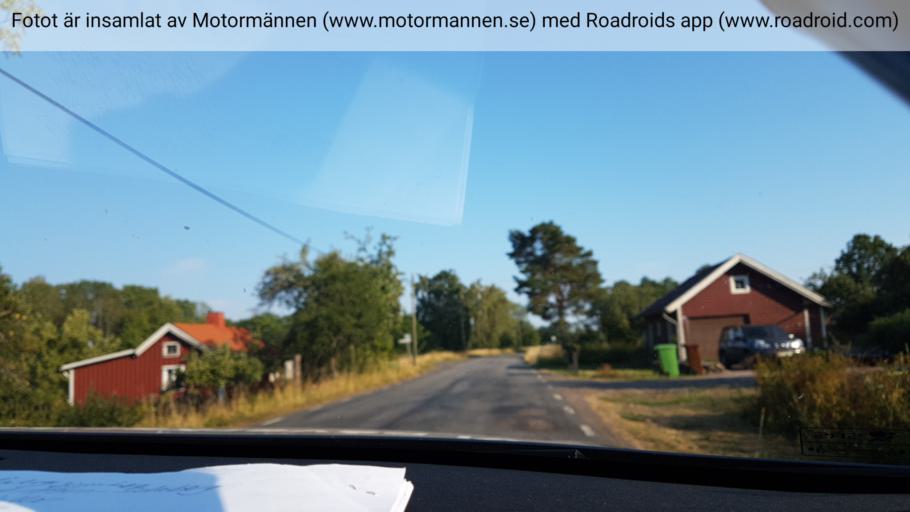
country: SE
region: Vaestra Goetaland
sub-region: Skovde Kommun
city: Stopen
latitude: 58.4900
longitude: 13.8342
